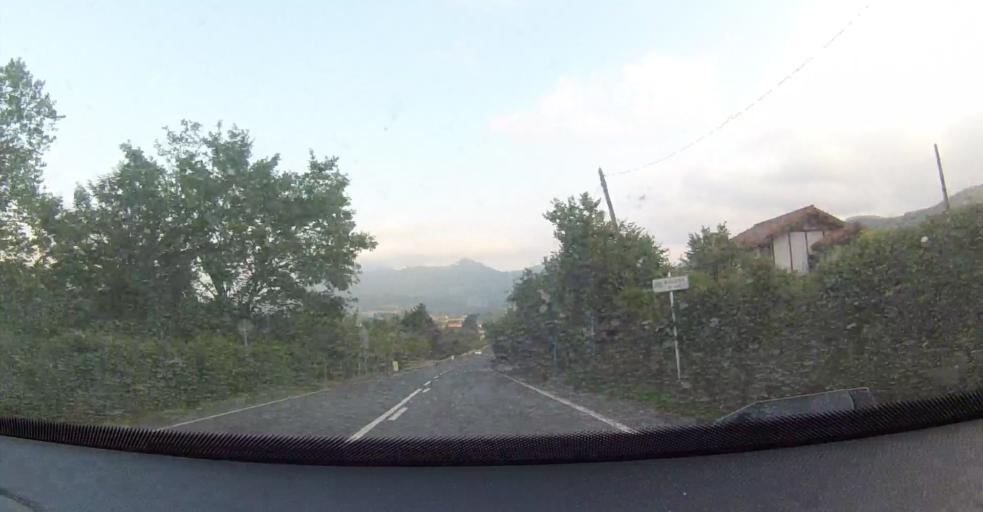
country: ES
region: Basque Country
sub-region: Bizkaia
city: Sopuerta
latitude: 43.2833
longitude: -3.1614
